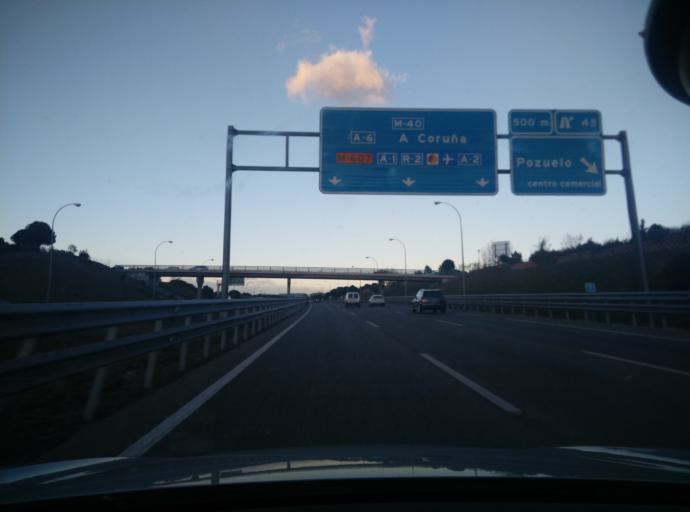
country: ES
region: Madrid
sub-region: Provincia de Madrid
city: Pozuelo de Alarcon
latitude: 40.4517
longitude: -3.8187
